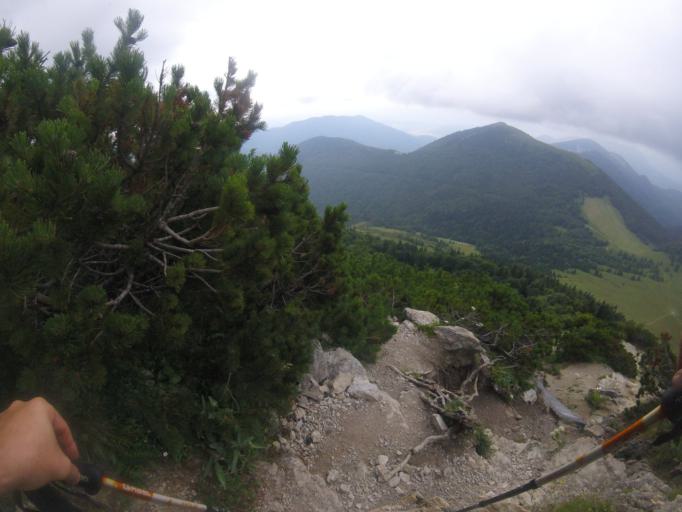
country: SK
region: Zilinsky
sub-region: Okres Zilina
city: Terchova
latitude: 49.2298
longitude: 19.1015
